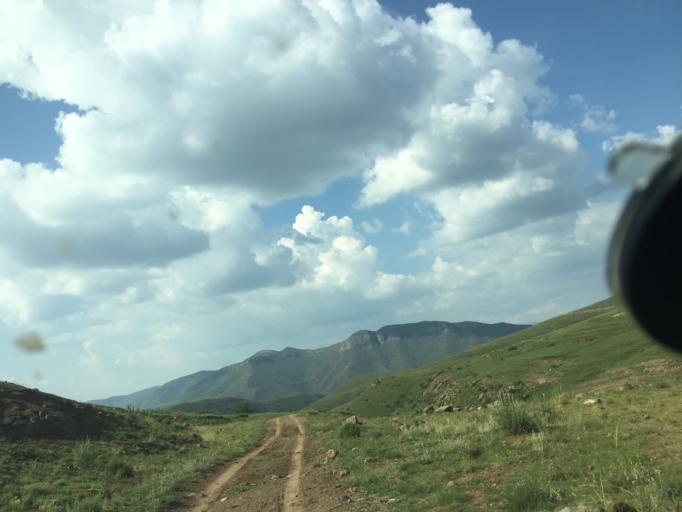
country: LS
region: Maseru
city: Nako
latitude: -29.6322
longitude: 28.1070
